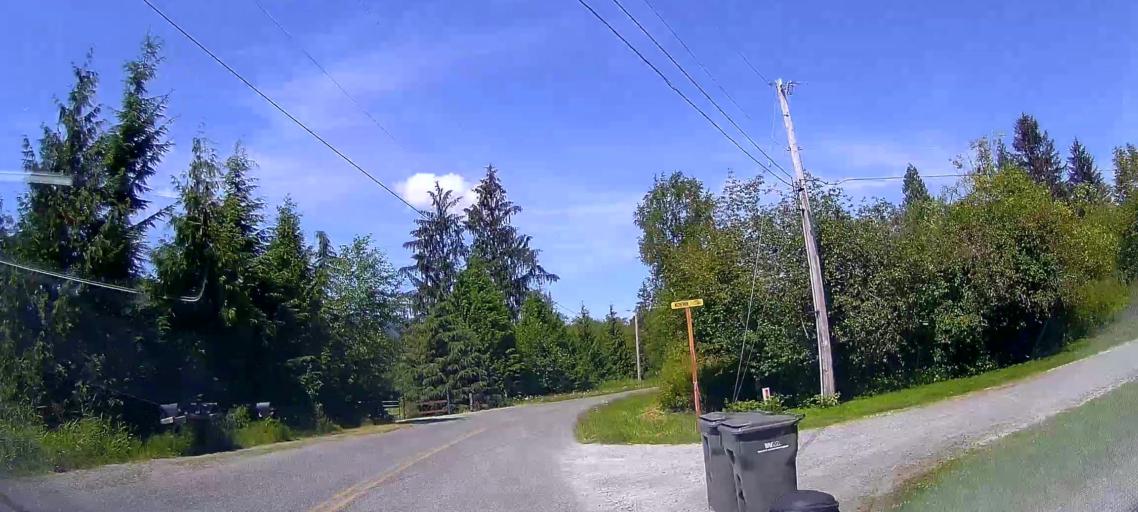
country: US
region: Washington
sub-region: Whatcom County
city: Sudden Valley
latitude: 48.6223
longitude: -122.3216
